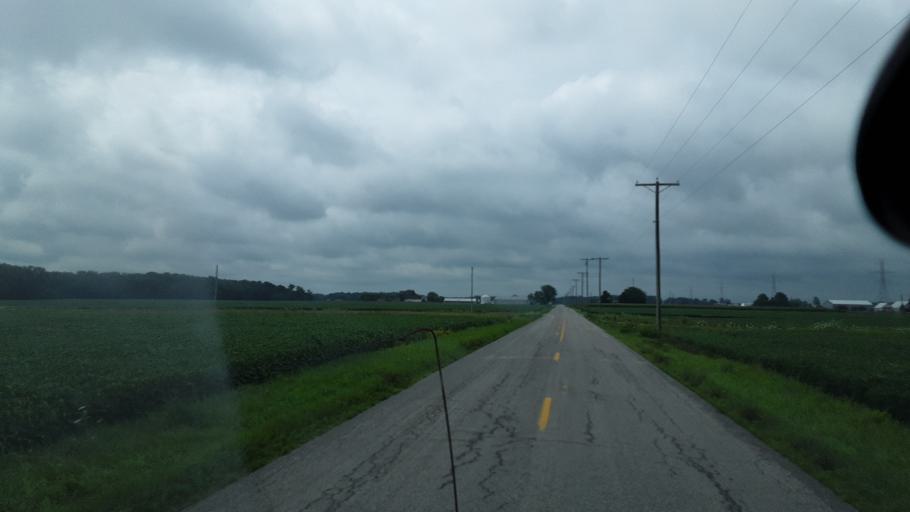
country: US
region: Indiana
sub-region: Allen County
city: Monroeville
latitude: 40.9647
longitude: -84.9690
